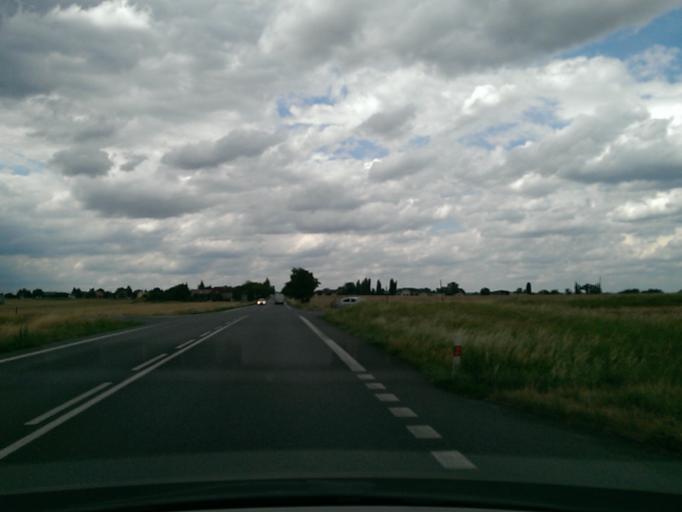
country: CZ
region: Central Bohemia
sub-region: Okres Nymburk
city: Nymburk
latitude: 50.2120
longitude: 15.0325
